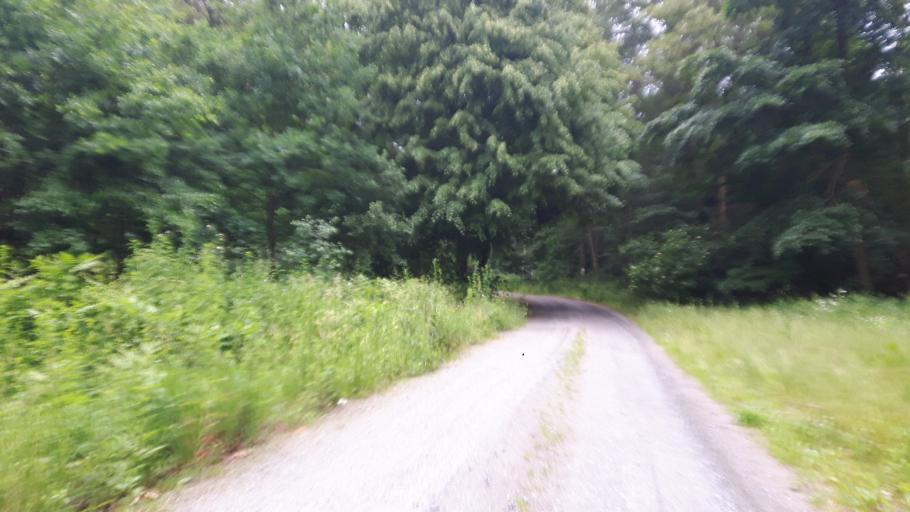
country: PL
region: Warmian-Masurian Voivodeship
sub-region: Powiat elblaski
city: Tolkmicko
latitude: 54.3354
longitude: 19.5668
